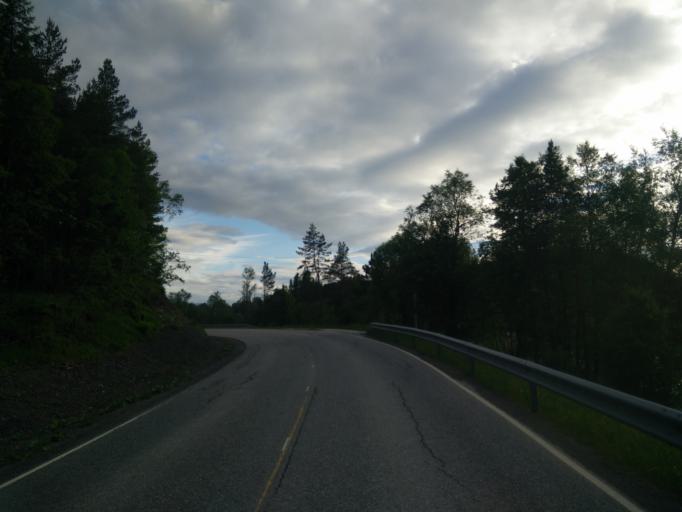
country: NO
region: More og Romsdal
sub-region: Tingvoll
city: Tingvoll
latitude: 63.0297
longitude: 8.0249
